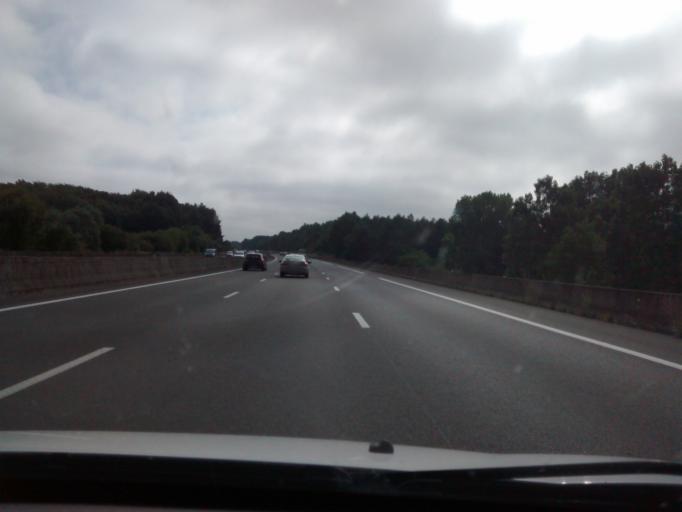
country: FR
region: Pays de la Loire
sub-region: Departement de la Sarthe
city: Connerre
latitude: 48.0752
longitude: 0.4707
